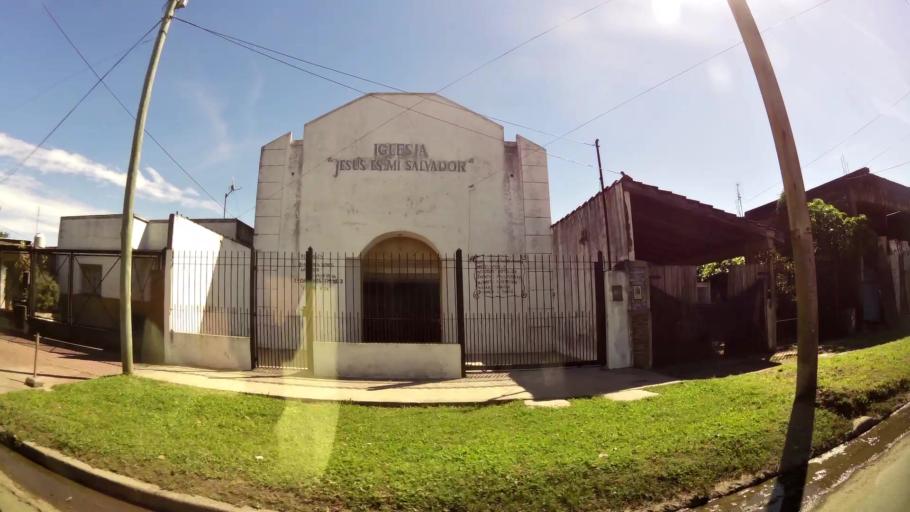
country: AR
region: Buenos Aires
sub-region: Partido de Almirante Brown
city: Adrogue
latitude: -34.7664
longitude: -58.3592
